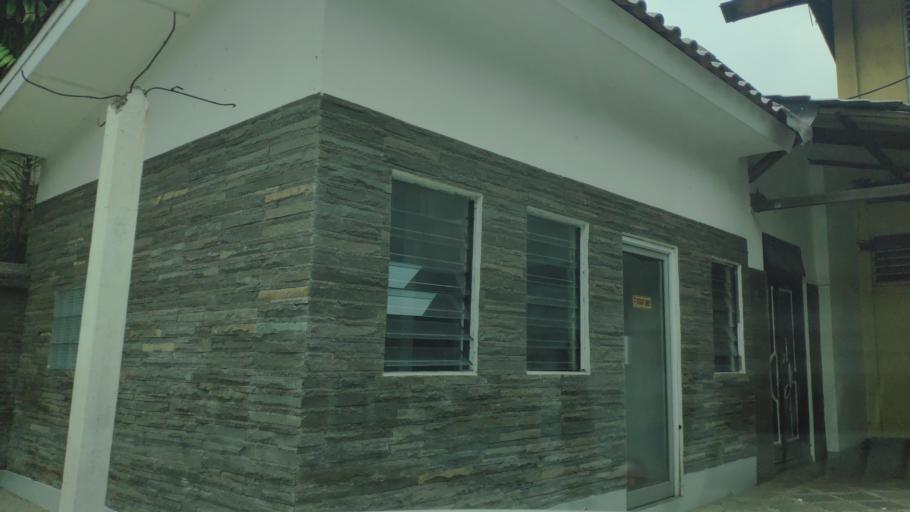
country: ID
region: Jakarta Raya
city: Jakarta
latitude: -6.1905
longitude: 106.7962
